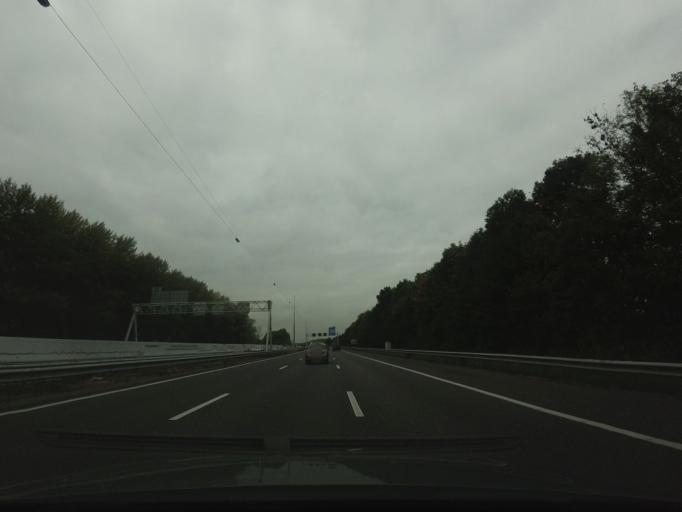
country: NL
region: North Holland
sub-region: Gemeente Waterland
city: Broek in Waterland
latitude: 52.3992
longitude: 4.9580
